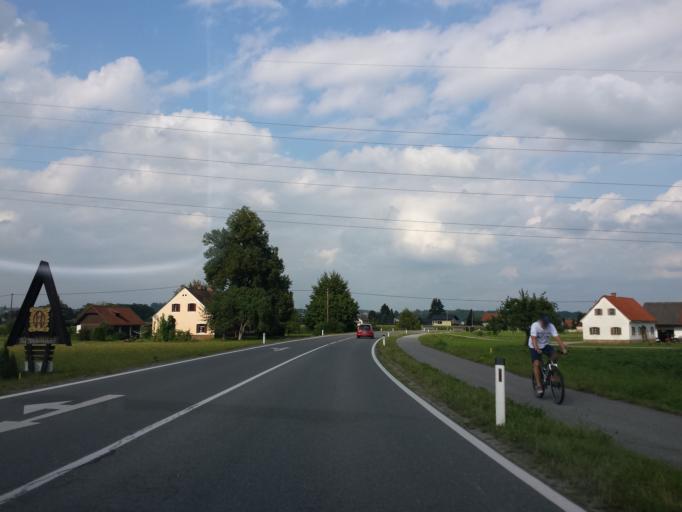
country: AT
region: Styria
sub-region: Politischer Bezirk Deutschlandsberg
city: Deutschlandsberg
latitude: 46.8188
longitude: 15.2474
